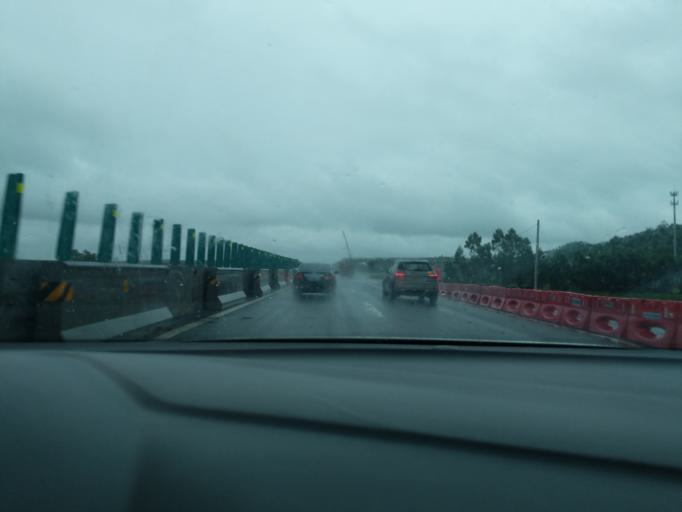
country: CN
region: Guangdong
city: Yueshan
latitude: 22.4637
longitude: 112.7122
